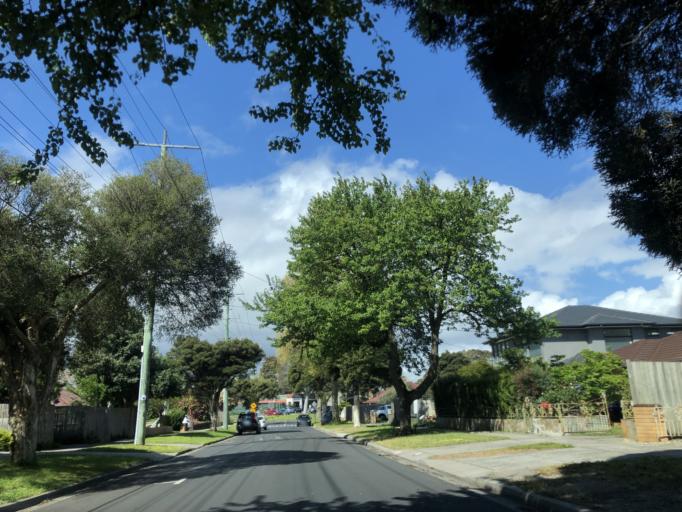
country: AU
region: Victoria
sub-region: Kingston
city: Clayton South
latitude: -37.9315
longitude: 145.1077
